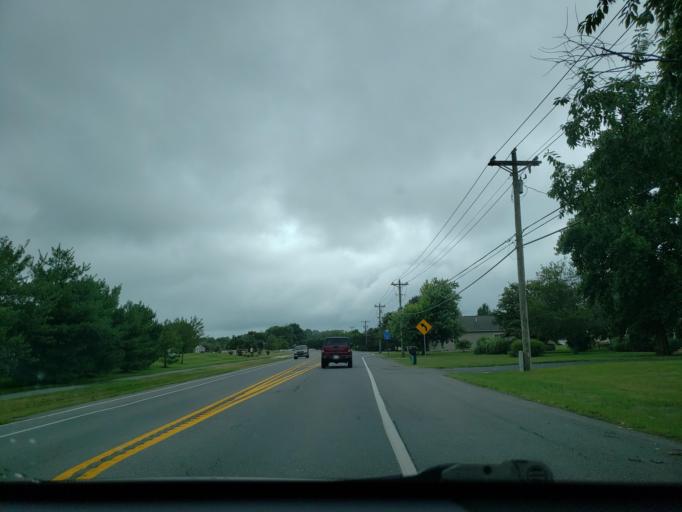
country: US
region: Delaware
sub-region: Sussex County
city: Milton
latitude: 38.7578
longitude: -75.2301
